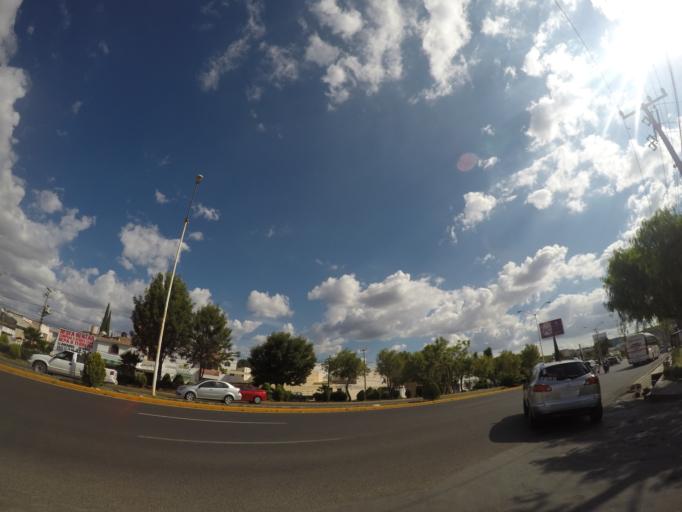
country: MX
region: San Luis Potosi
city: Escalerillas
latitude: 22.1348
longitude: -101.0297
